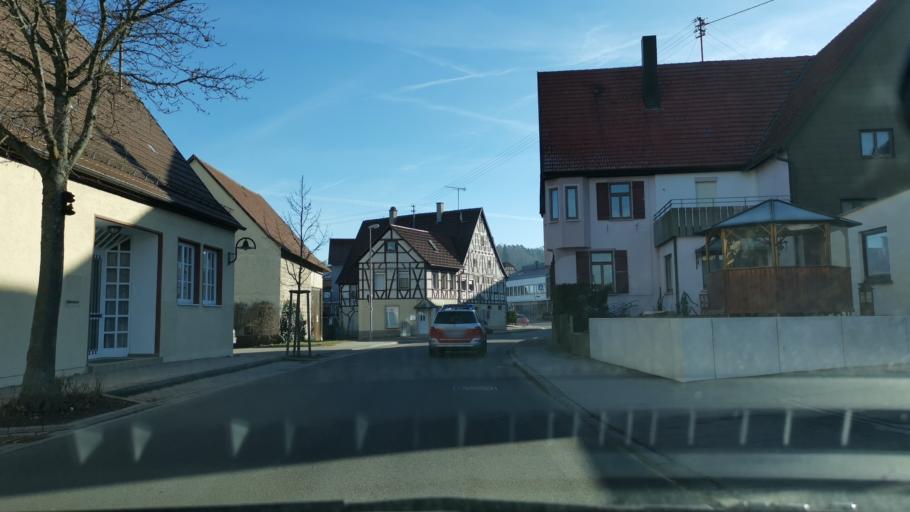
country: DE
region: Baden-Wuerttemberg
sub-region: Regierungsbezirk Stuttgart
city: Gartringen
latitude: 48.6251
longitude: 8.9219
